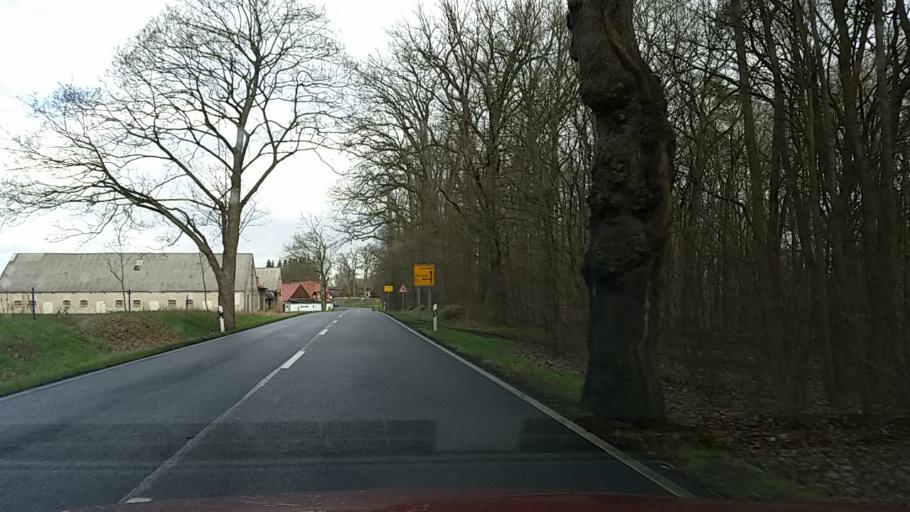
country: DE
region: Saxony-Anhalt
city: Rohrberg
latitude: 52.7300
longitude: 11.0574
